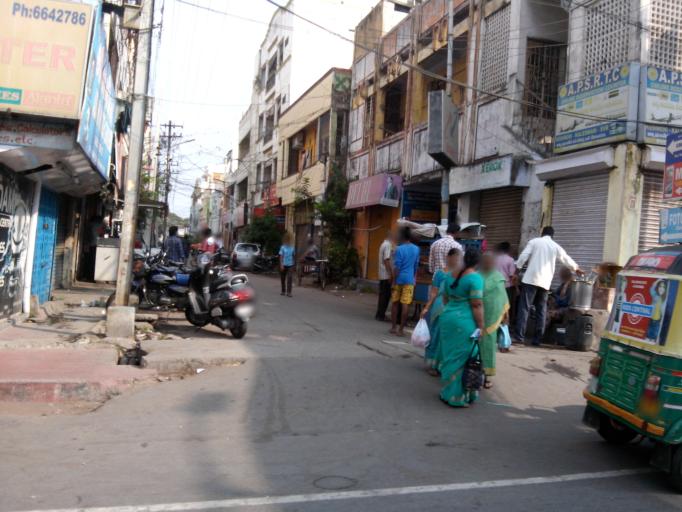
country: IN
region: Andhra Pradesh
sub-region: Krishna
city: Vijayawada
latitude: 16.5140
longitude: 80.6298
